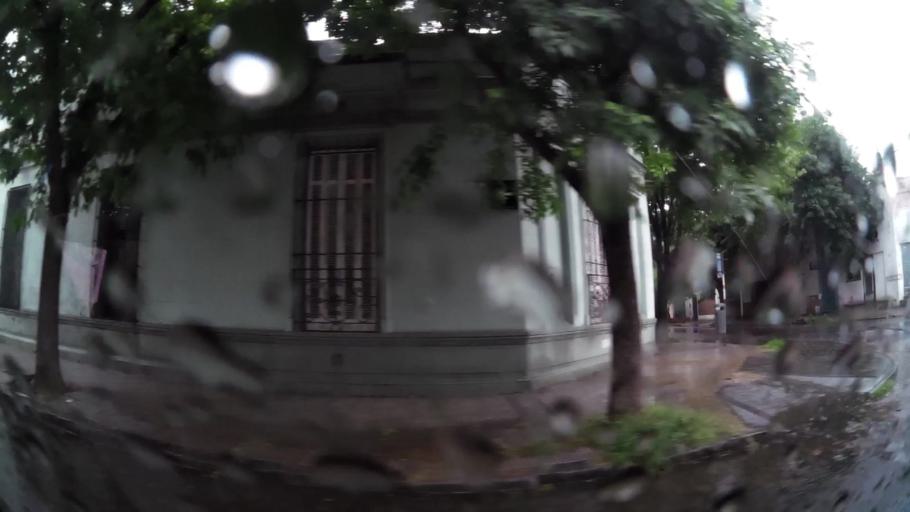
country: AR
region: Buenos Aires
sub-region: Partido de Avellaneda
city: Avellaneda
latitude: -34.6415
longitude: -58.3719
